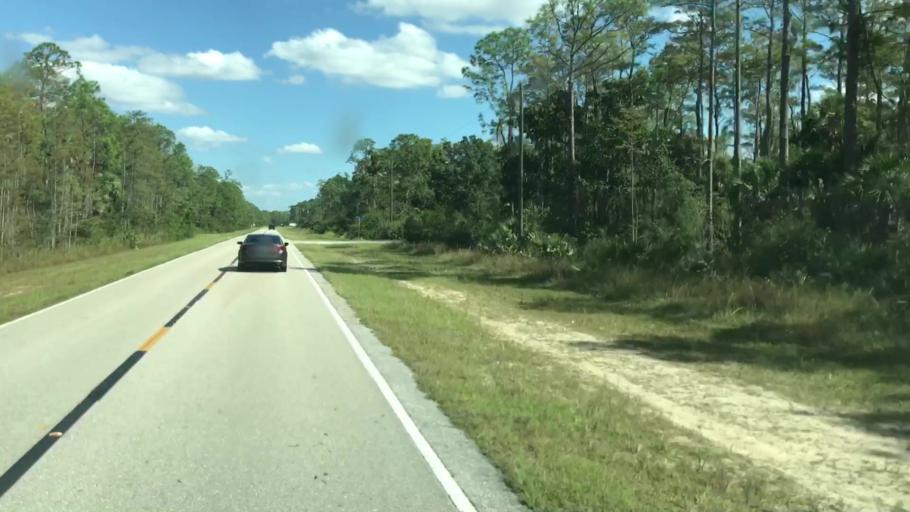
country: US
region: Florida
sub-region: Lee County
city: Alva
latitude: 26.6774
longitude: -81.6163
